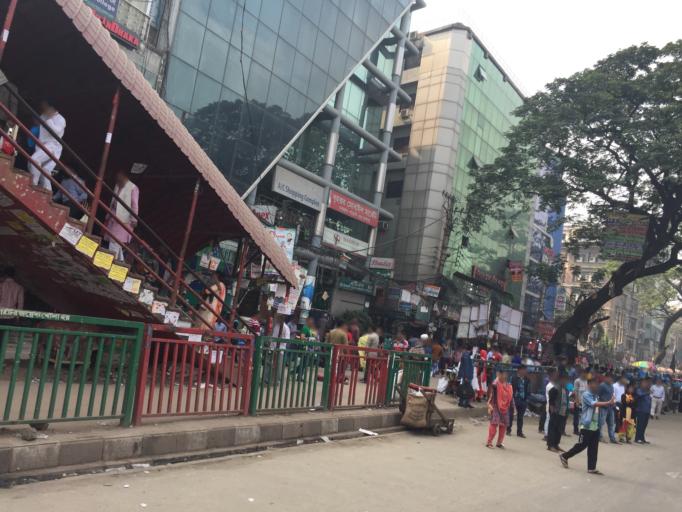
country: BD
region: Dhaka
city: Azimpur
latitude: 23.7584
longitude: 90.3897
